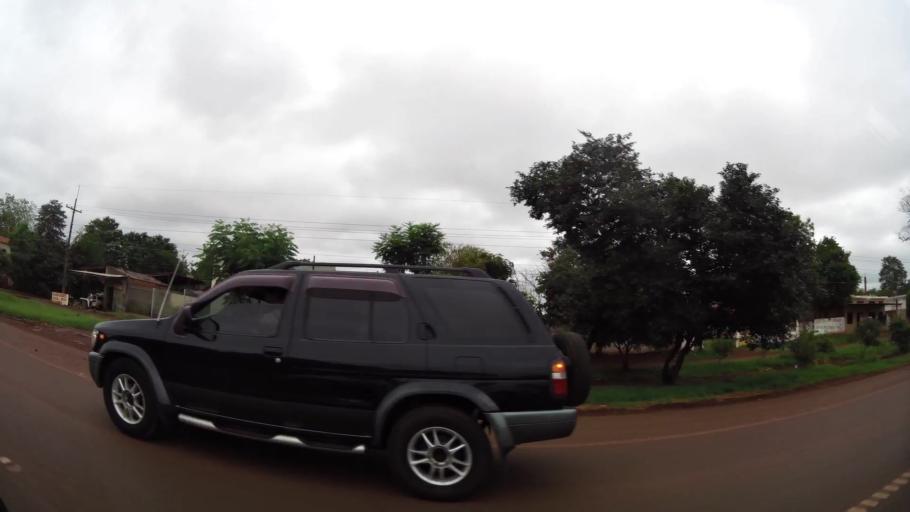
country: PY
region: Alto Parana
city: Los Cedrales
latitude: -25.4890
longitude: -54.8079
